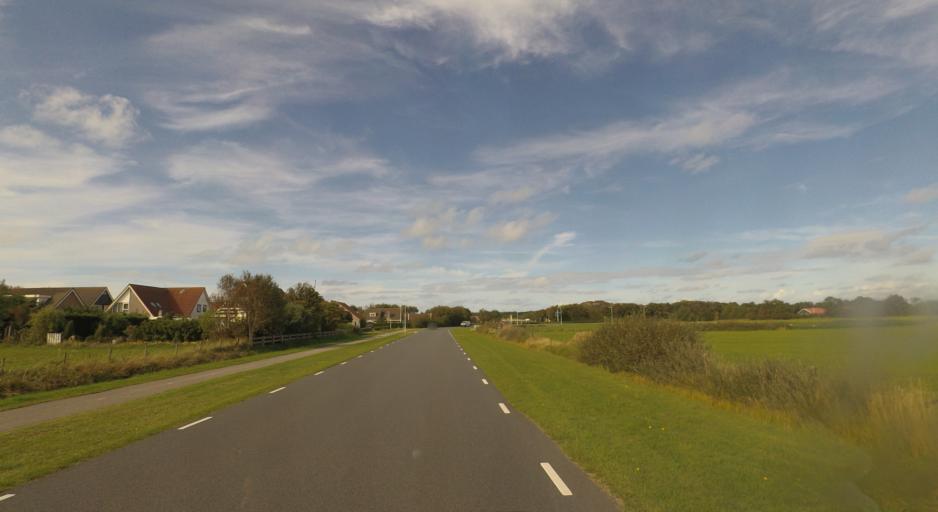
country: NL
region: Friesland
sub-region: Gemeente Ameland
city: Nes
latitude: 53.4450
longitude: 5.7820
